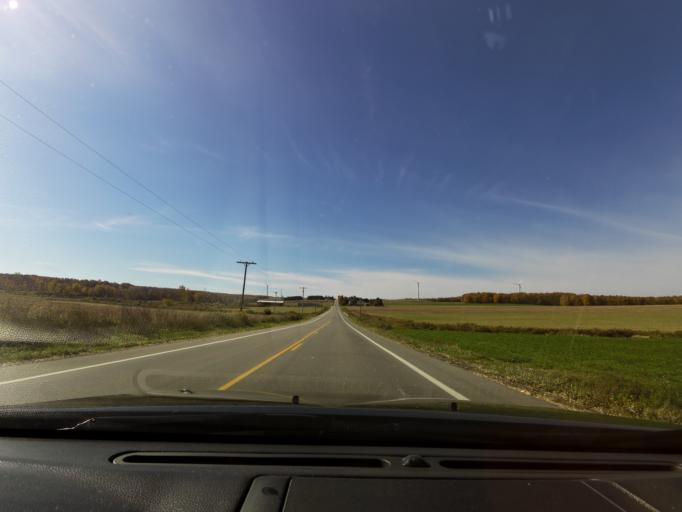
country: US
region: New York
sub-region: Wyoming County
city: Warsaw
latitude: 42.6435
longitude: -78.2136
